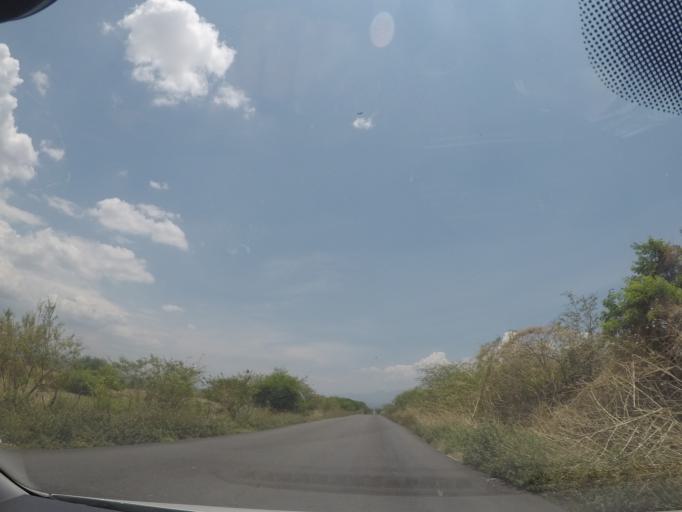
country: MX
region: Oaxaca
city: Santa Maria Jalapa del Marques
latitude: 16.4397
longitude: -95.4729
